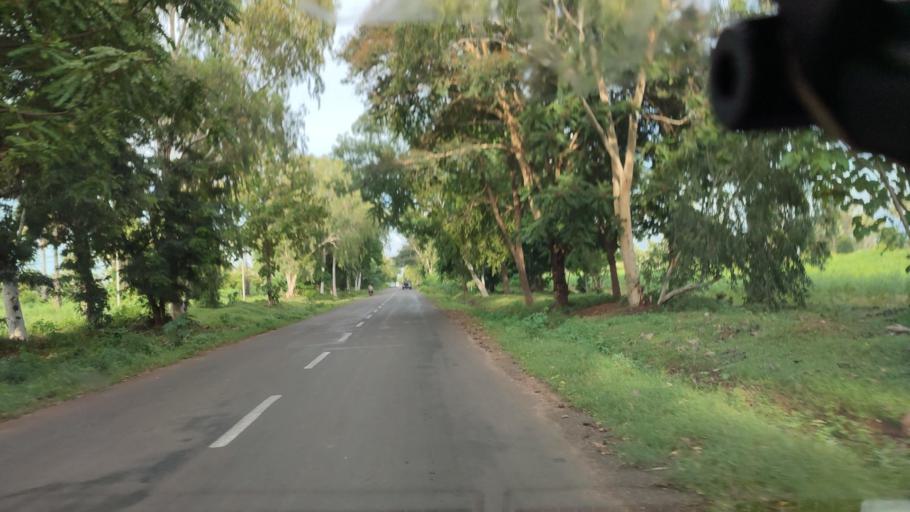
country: MM
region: Magway
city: Chauk
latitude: 20.8109
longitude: 95.0429
